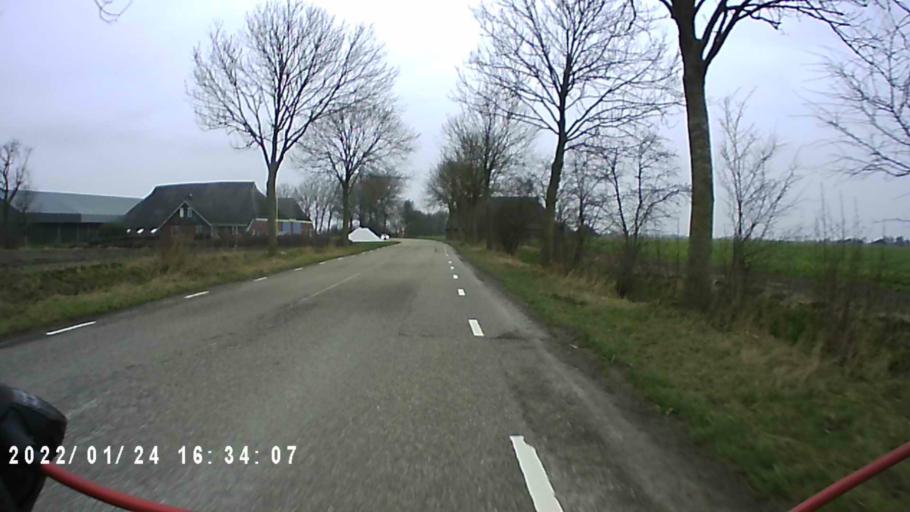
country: NL
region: Groningen
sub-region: Gemeente Zuidhorn
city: Oldehove
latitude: 53.3774
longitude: 6.4209
